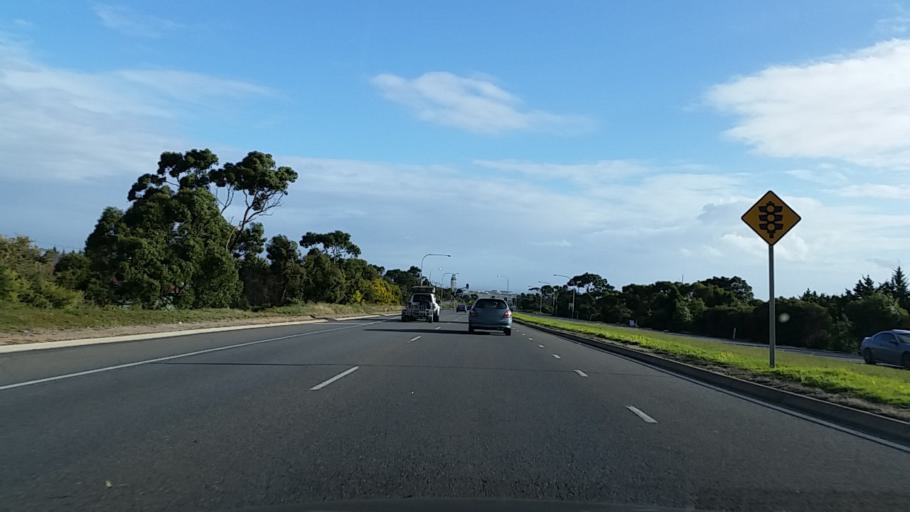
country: AU
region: South Australia
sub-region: Marion
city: Happy Valley
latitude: -35.0705
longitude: 138.5272
